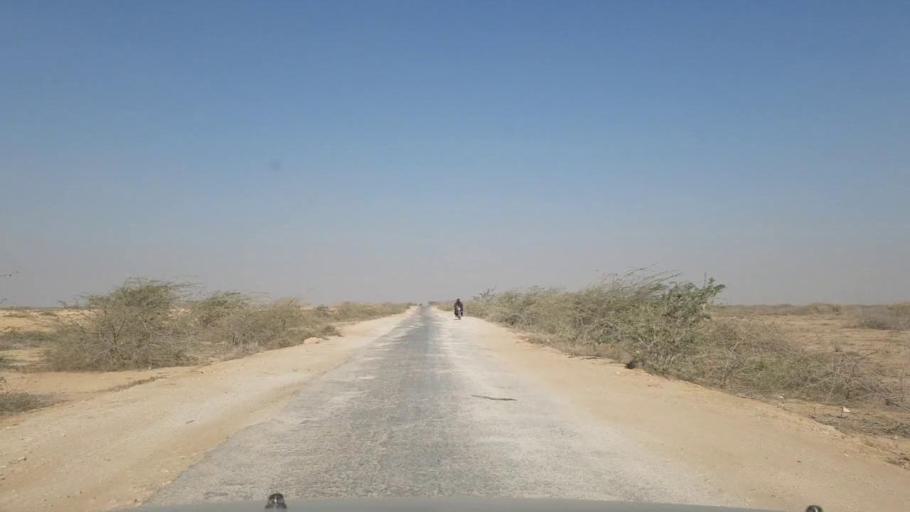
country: PK
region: Sindh
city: Thatta
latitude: 24.8354
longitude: 67.8901
